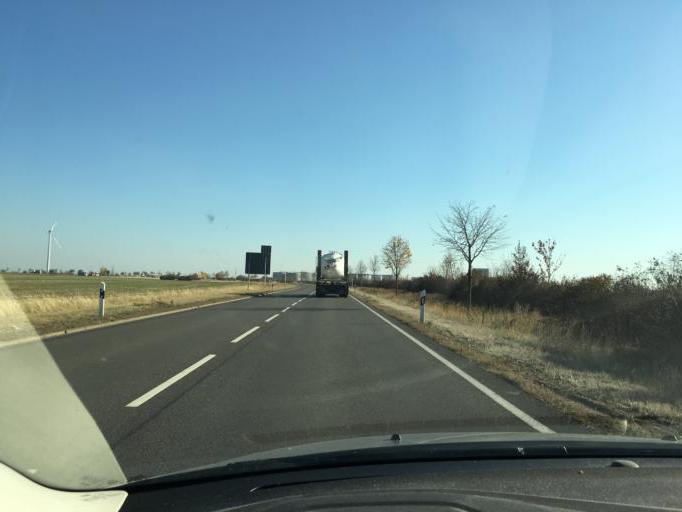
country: DE
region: Saxony-Anhalt
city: Zorbig
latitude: 51.6351
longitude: 12.1335
